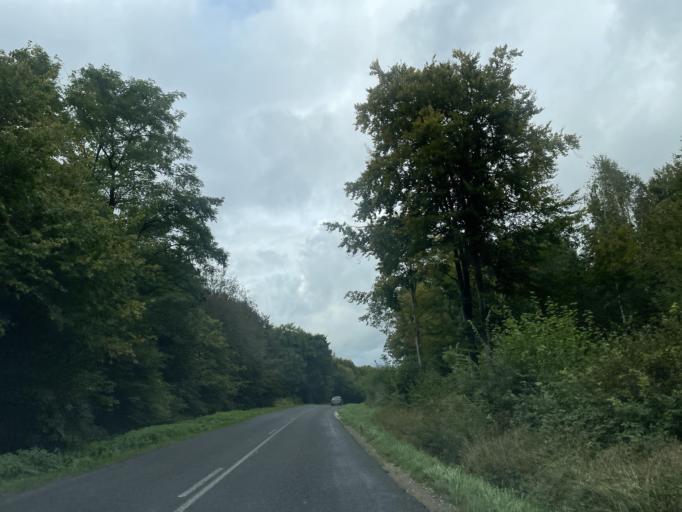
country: FR
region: Ile-de-France
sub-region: Departement de Seine-et-Marne
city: Saint-Jean-les-Deux-Jumeaux
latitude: 48.9150
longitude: 3.0138
